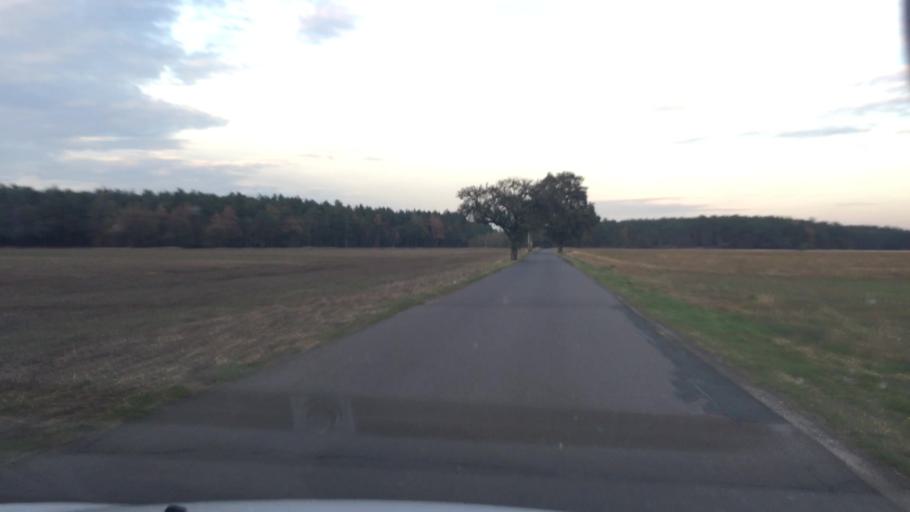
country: DE
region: Brandenburg
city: Welzow
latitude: 51.5600
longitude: 14.1362
